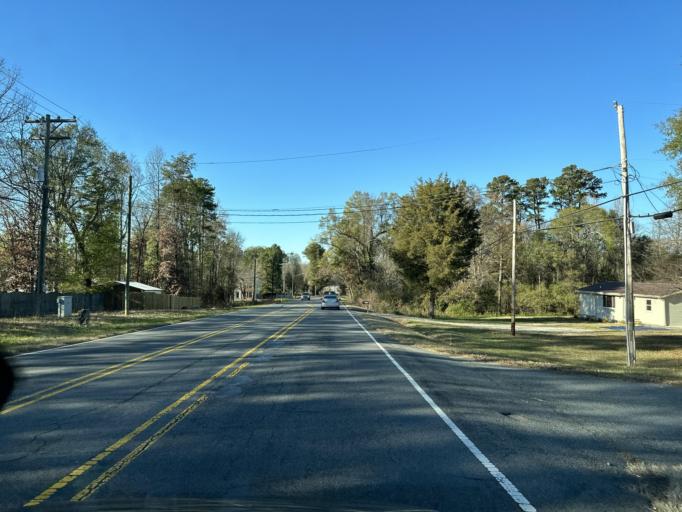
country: US
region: North Carolina
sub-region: Gaston County
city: Mount Holly
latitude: 35.3110
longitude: -80.9404
